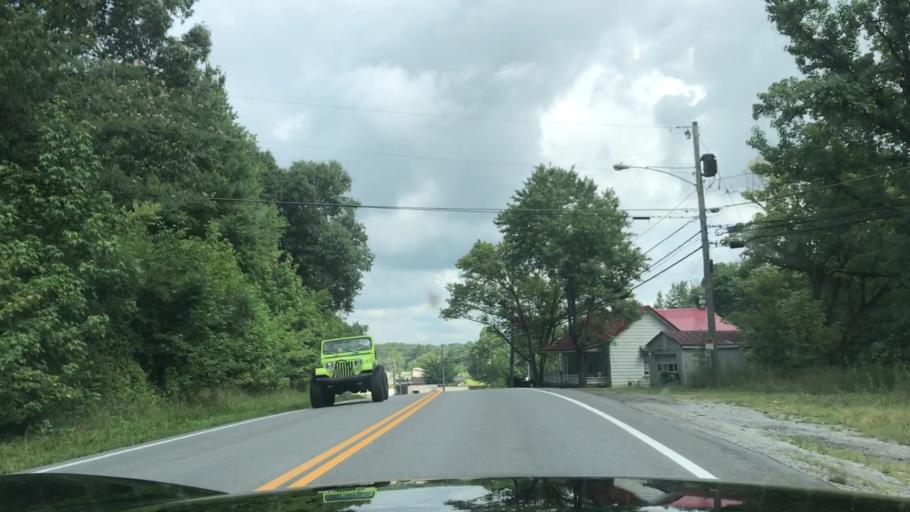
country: US
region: Kentucky
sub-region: Muhlenberg County
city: Central City
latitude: 37.2166
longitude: -87.0450
